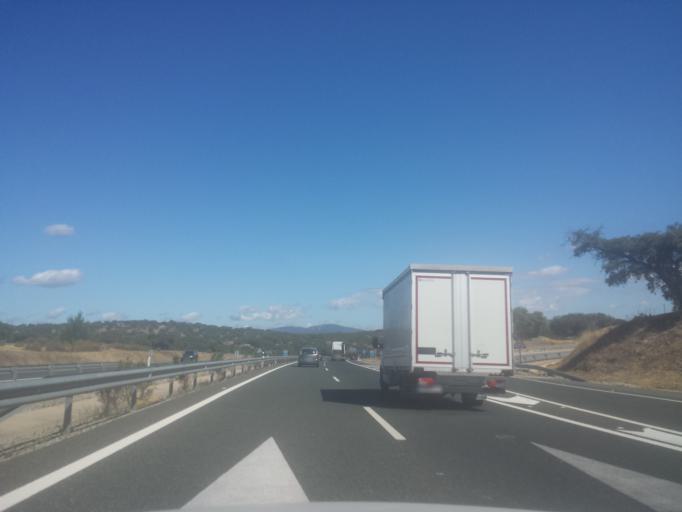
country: ES
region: Andalusia
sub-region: Provincia de Huelva
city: Santa Olalla del Cala
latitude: 37.9187
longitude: -6.2238
